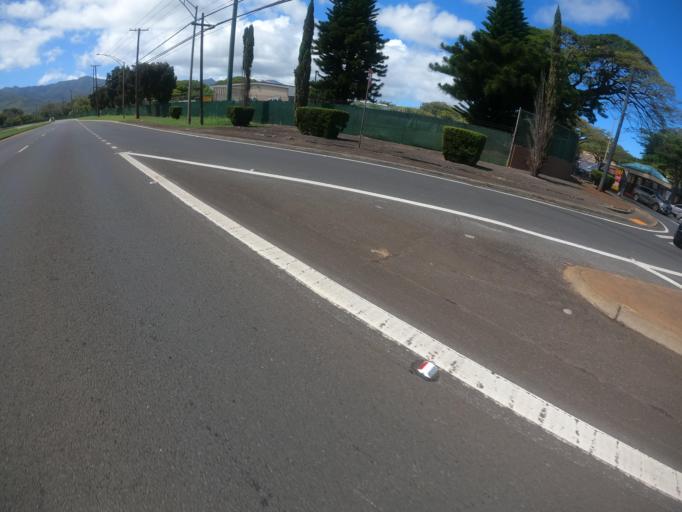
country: US
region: Hawaii
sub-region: Honolulu County
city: Schofield Barracks
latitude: 21.4848
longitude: -158.0450
